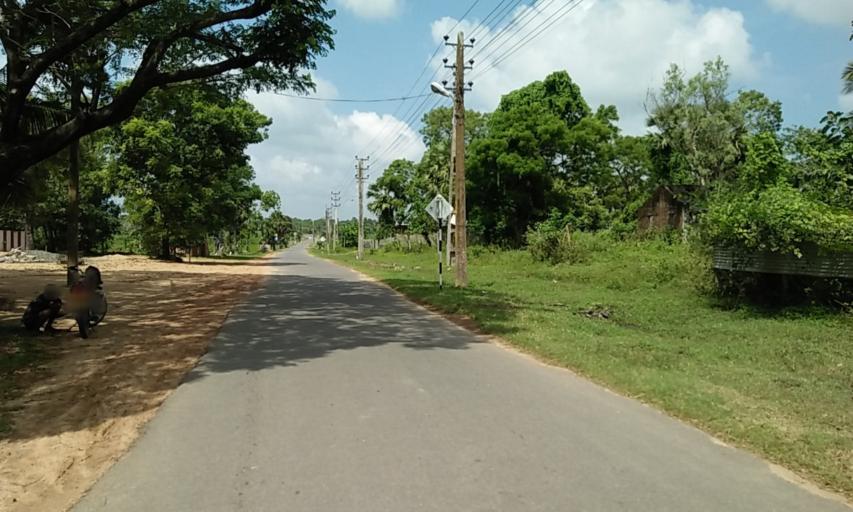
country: LK
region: Eastern Province
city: Ampara
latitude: 7.3376
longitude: 81.7428
